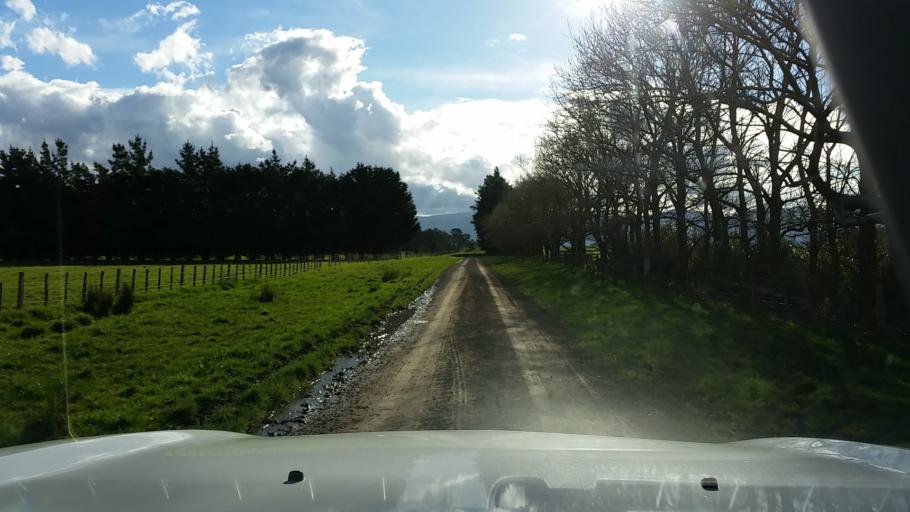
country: NZ
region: Wellington
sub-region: Upper Hutt City
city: Upper Hutt
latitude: -41.2396
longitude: 175.3006
